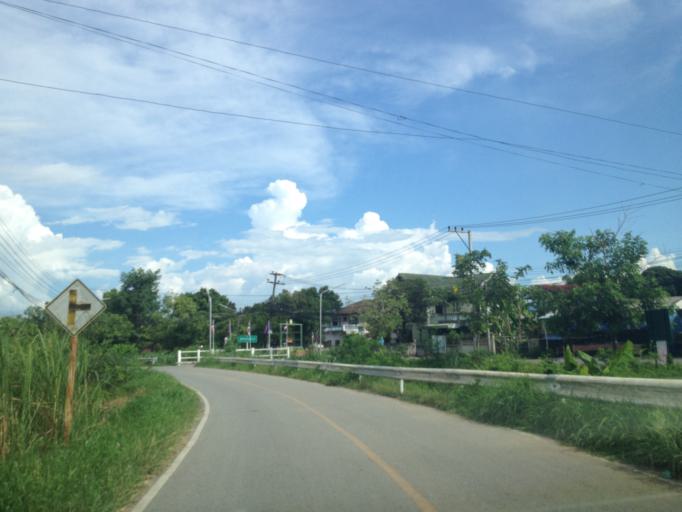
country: TH
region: Chiang Mai
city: Chiang Mai
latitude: 18.7461
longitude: 98.9439
